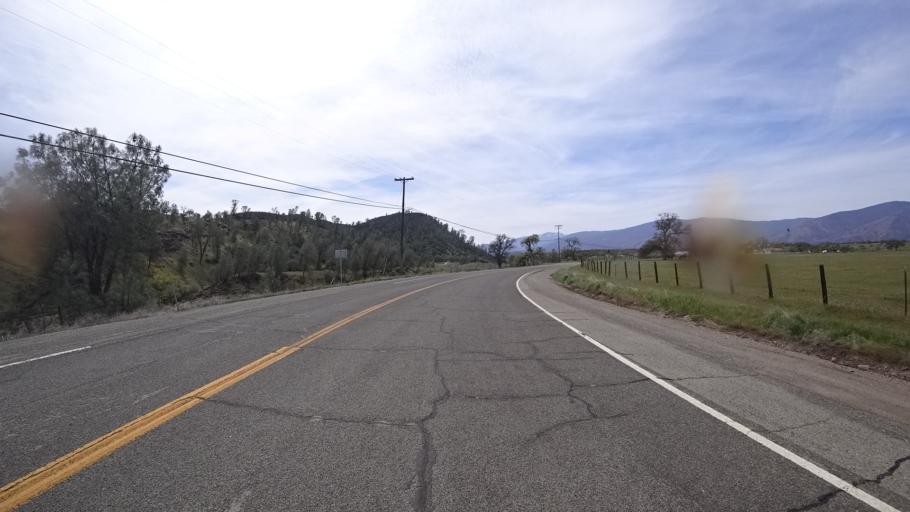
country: US
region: California
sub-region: Glenn County
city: Willows
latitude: 39.6111
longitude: -122.5307
